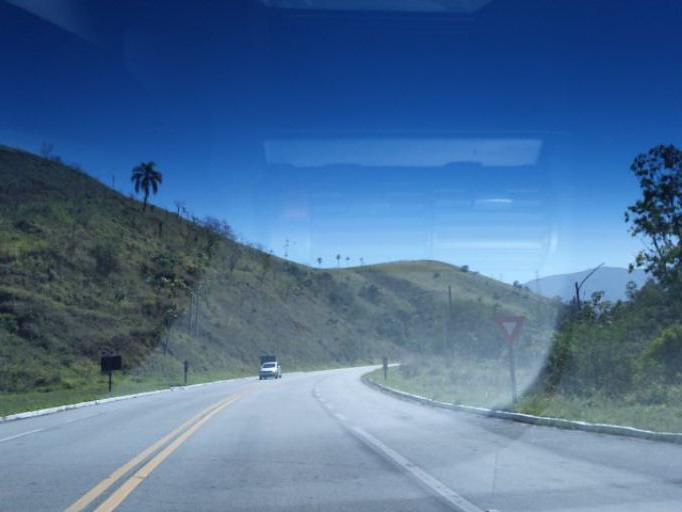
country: BR
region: Sao Paulo
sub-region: Tremembe
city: Tremembe
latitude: -22.8896
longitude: -45.5966
